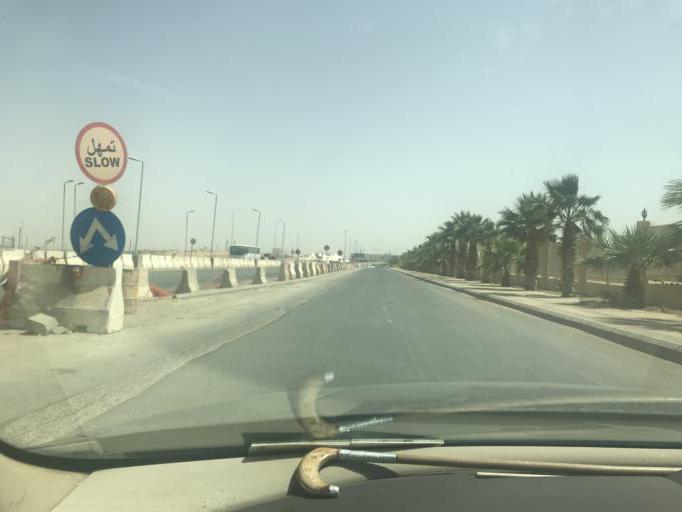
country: SA
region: Ar Riyad
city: Riyadh
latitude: 24.8279
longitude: 46.6953
